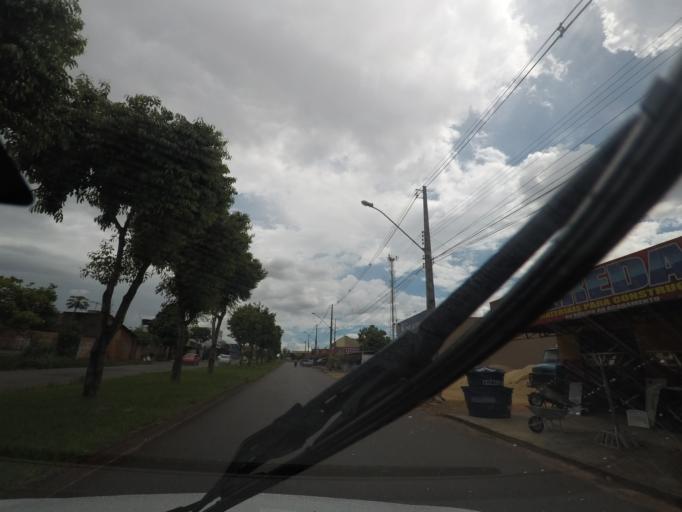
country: BR
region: Goias
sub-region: Goiania
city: Goiania
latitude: -16.7255
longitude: -49.3385
